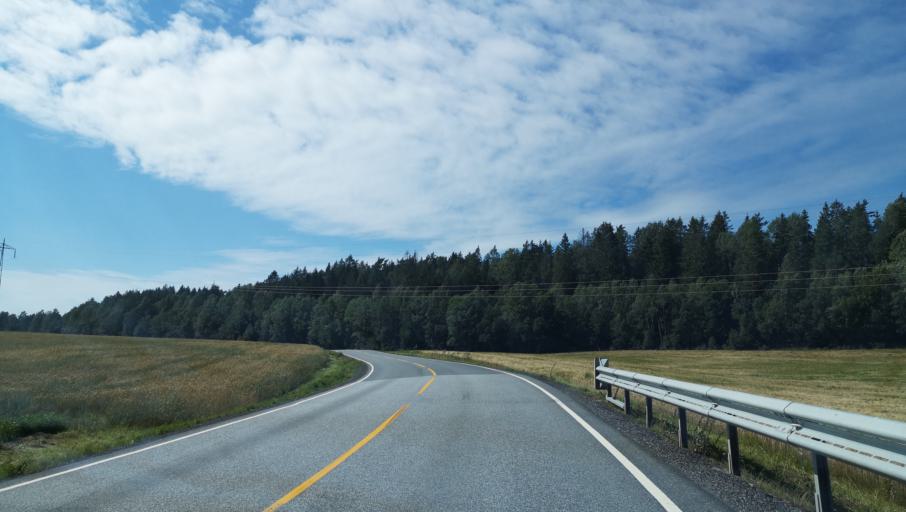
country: NO
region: Akershus
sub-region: Vestby
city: Vestby
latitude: 59.5433
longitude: 10.7824
